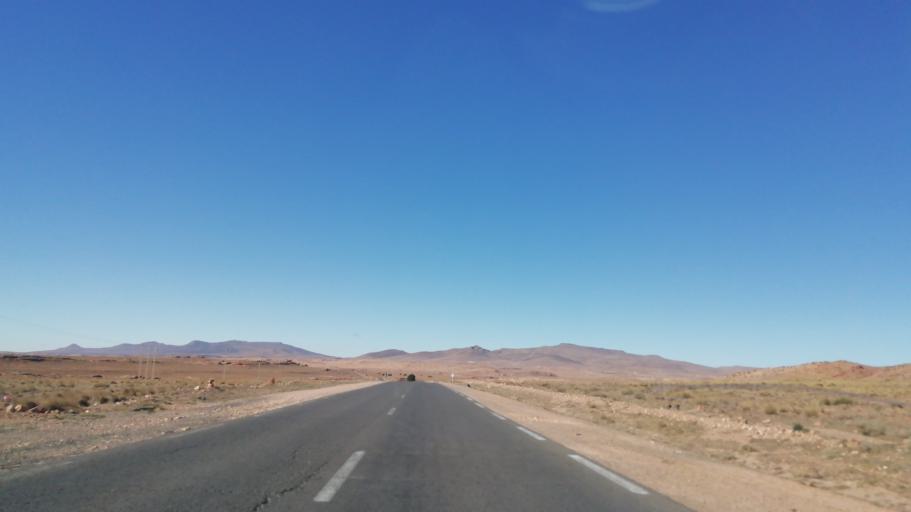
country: DZ
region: El Bayadh
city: El Bayadh
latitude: 33.6119
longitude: 1.2256
